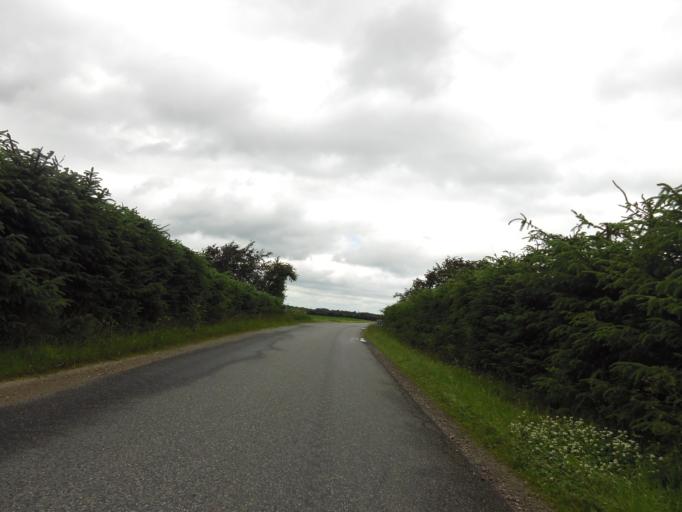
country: DK
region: South Denmark
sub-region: Kolding Kommune
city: Vamdrup
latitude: 55.3442
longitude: 9.1983
